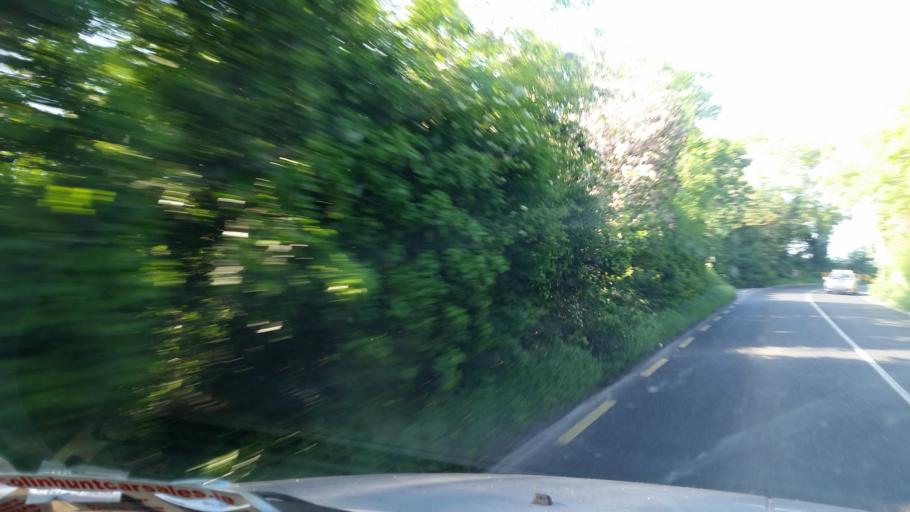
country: IE
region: Leinster
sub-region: Fingal County
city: Blanchardstown
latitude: 53.4217
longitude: -6.3396
